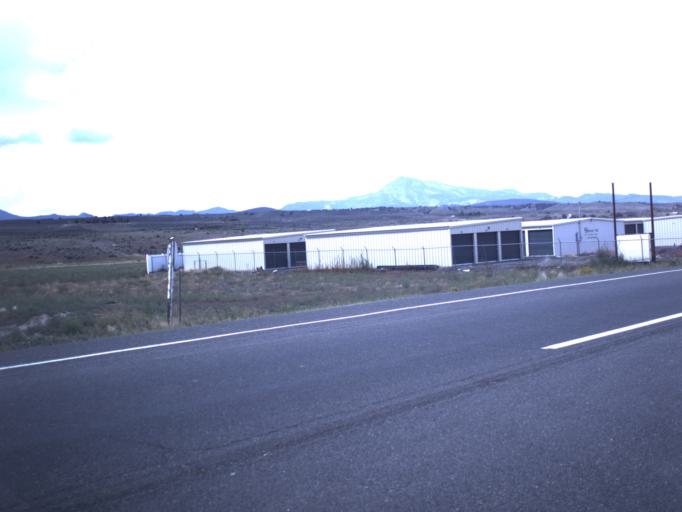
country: US
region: Utah
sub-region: Garfield County
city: Panguitch
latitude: 37.8351
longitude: -112.4377
